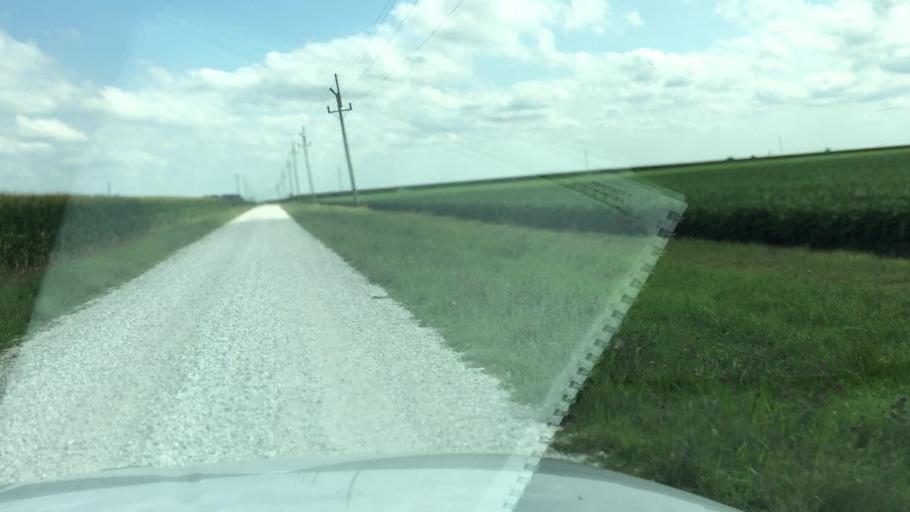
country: US
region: Illinois
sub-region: Hancock County
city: Carthage
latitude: 40.4085
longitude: -91.1786
